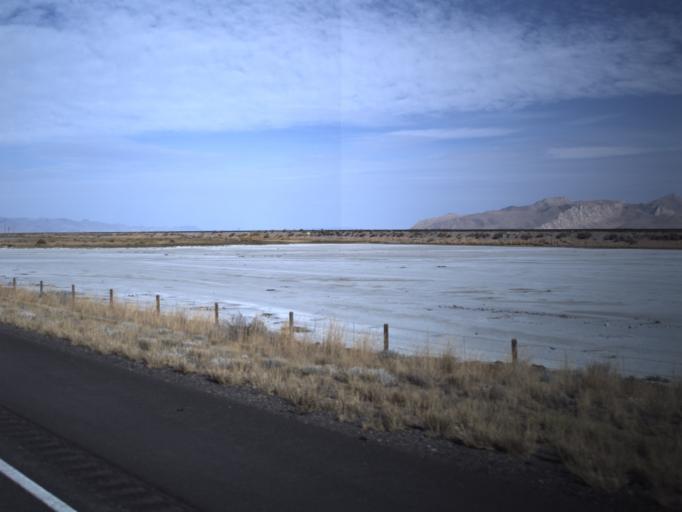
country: US
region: Utah
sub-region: Tooele County
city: Grantsville
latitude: 40.6816
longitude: -112.4255
